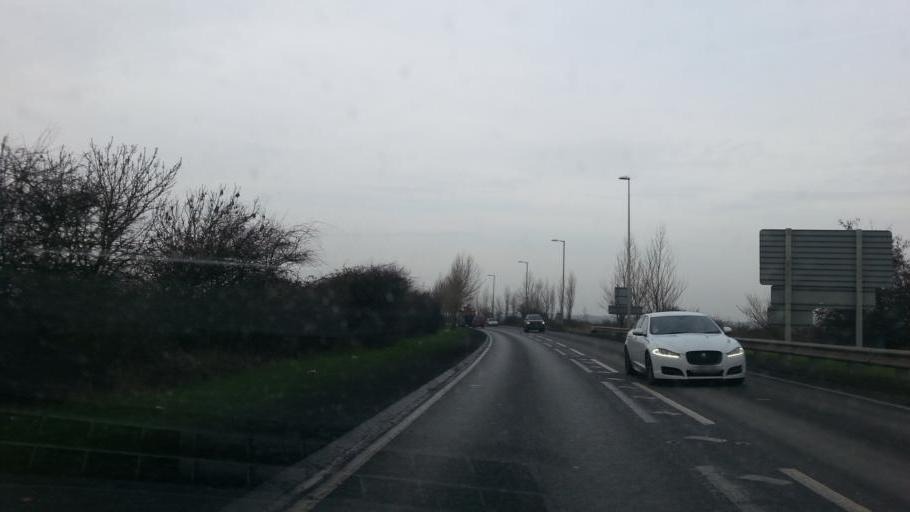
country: GB
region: England
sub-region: Essex
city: South Benfleet
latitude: 51.5375
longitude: 0.5620
